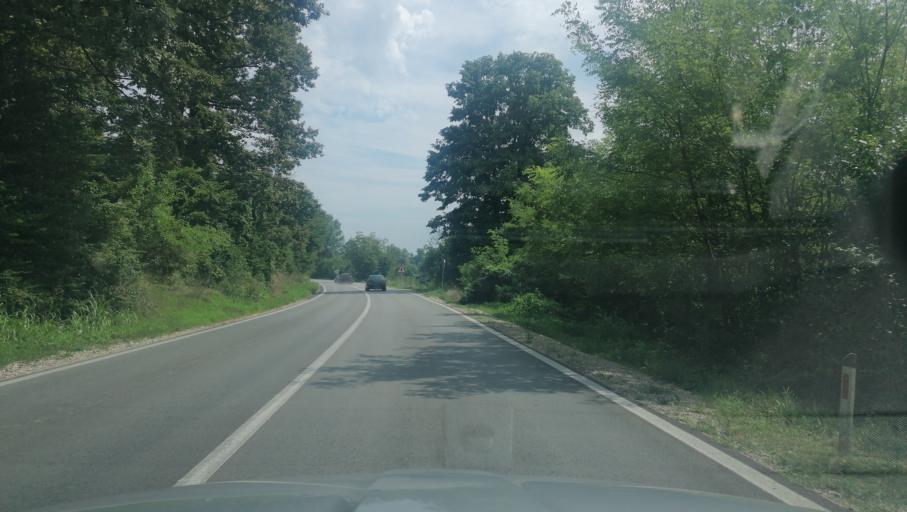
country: BA
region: Federation of Bosnia and Herzegovina
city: Odzak
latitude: 44.9668
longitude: 18.2369
